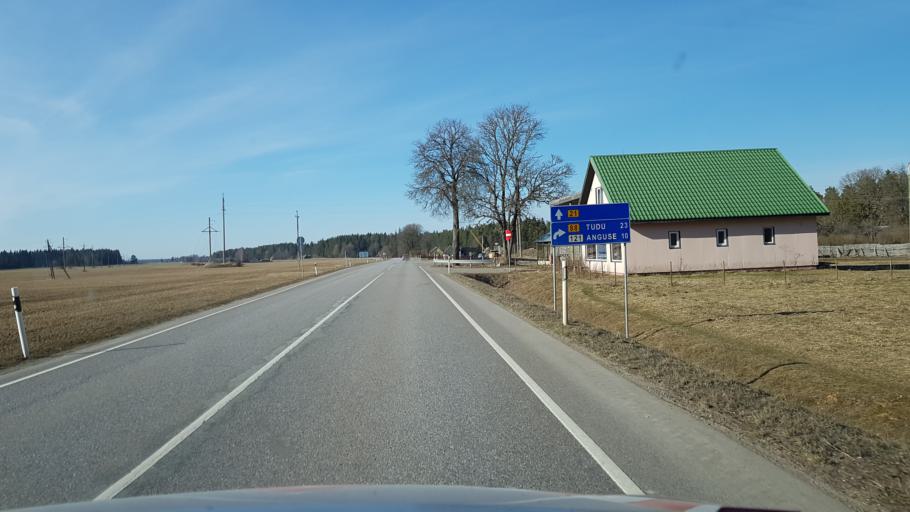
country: EE
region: Laeaene-Virumaa
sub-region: Vinni vald
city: Vinni
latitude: 59.1794
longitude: 26.5775
